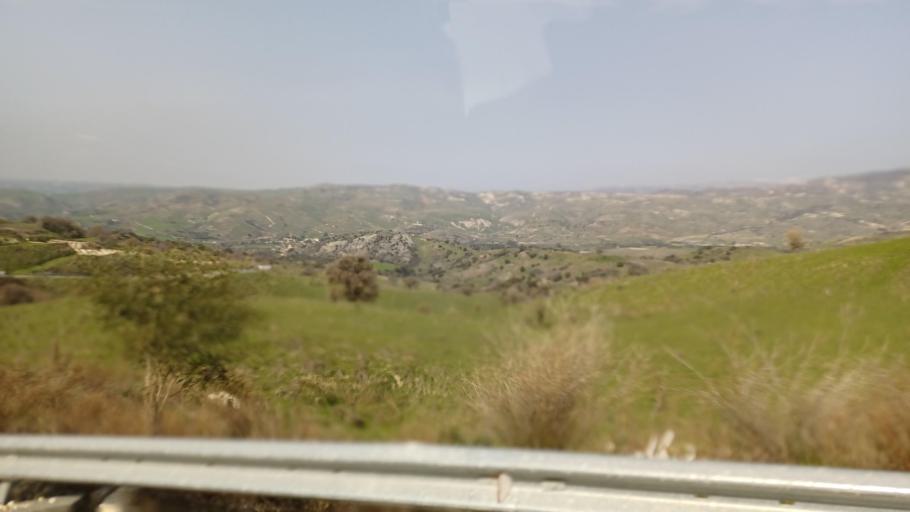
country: CY
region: Limassol
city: Pissouri
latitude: 34.7533
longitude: 32.6541
